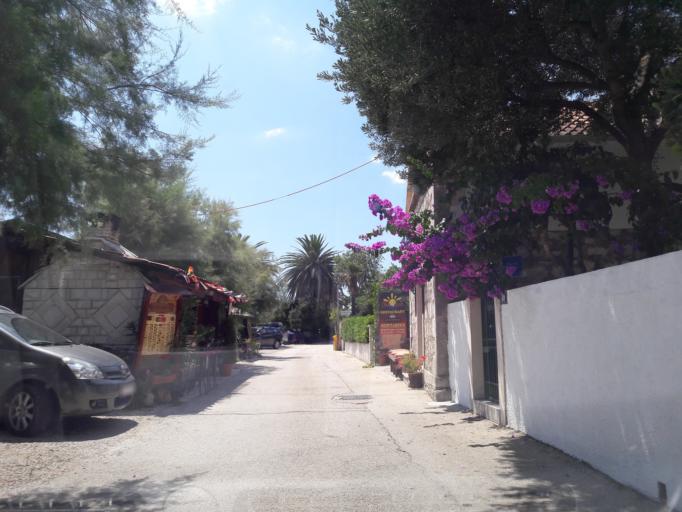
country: HR
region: Dubrovacko-Neretvanska
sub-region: Grad Korcula
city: Zrnovo
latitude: 42.9846
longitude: 17.0921
